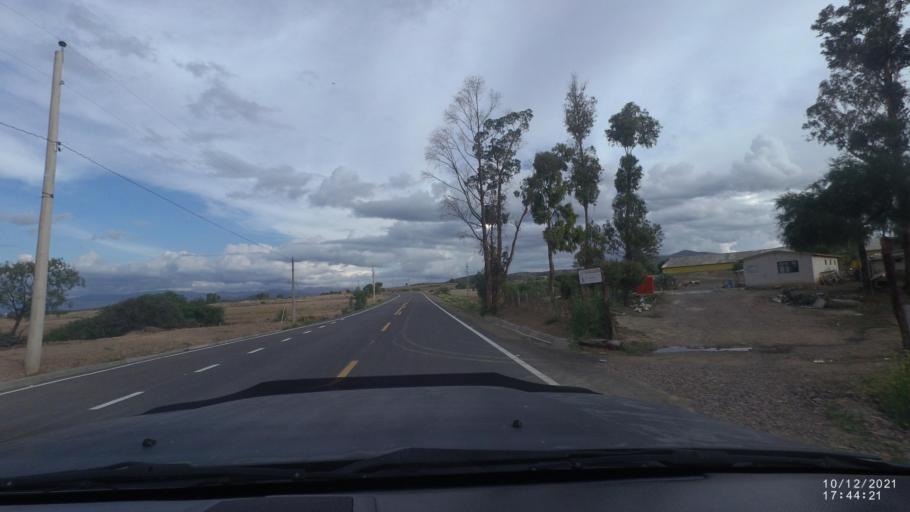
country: BO
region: Cochabamba
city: Tarata
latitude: -17.6194
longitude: -66.0138
